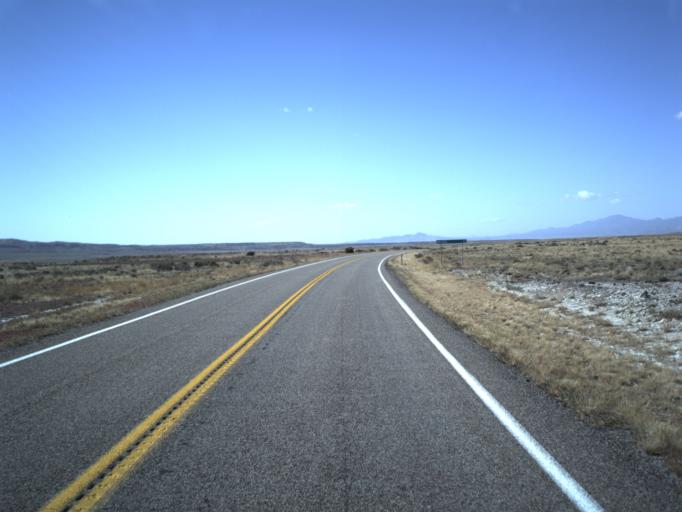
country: US
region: Utah
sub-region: Beaver County
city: Milford
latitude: 38.8259
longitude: -112.8515
